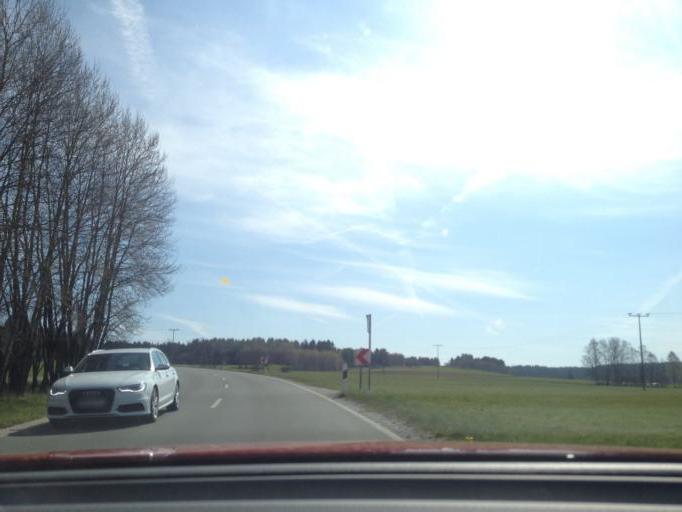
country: DE
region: Bavaria
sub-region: Upper Franconia
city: Oberhaid
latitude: 50.0942
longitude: 11.7949
